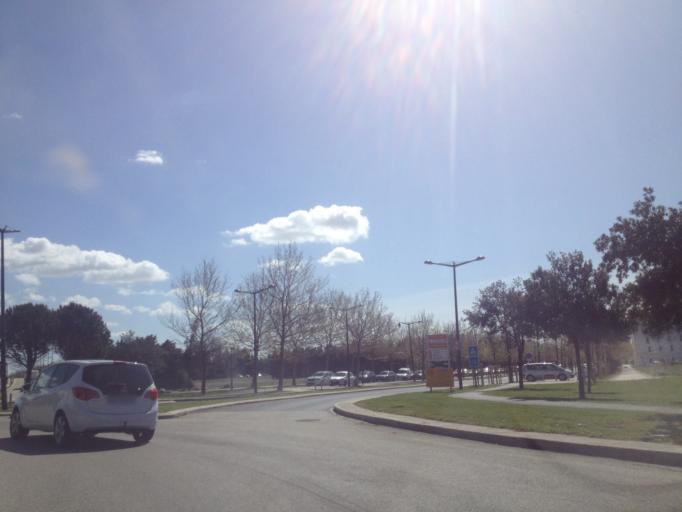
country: FR
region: Provence-Alpes-Cote d'Azur
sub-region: Departement du Vaucluse
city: Avignon
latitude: 43.9285
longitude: 4.7848
